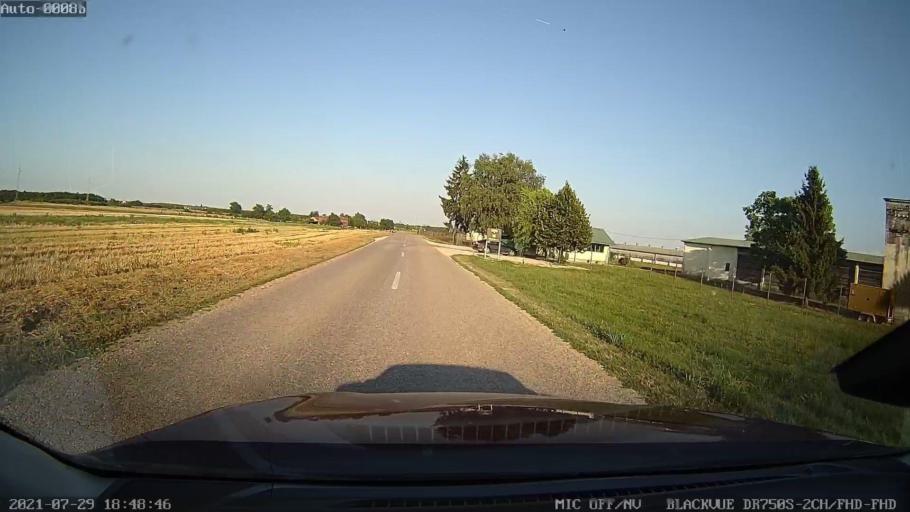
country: HR
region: Varazdinska
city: Sracinec
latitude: 46.3109
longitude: 16.2947
